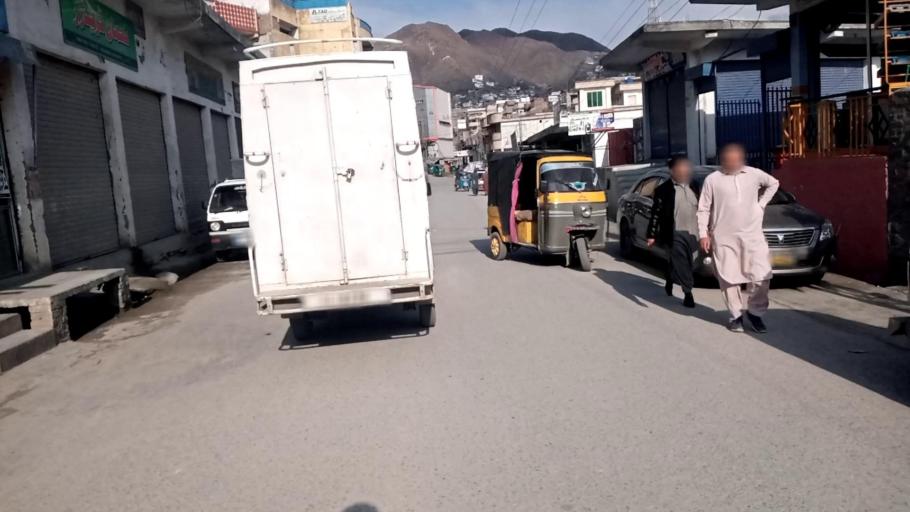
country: PK
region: Khyber Pakhtunkhwa
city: Mingora
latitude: 34.7753
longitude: 72.3636
